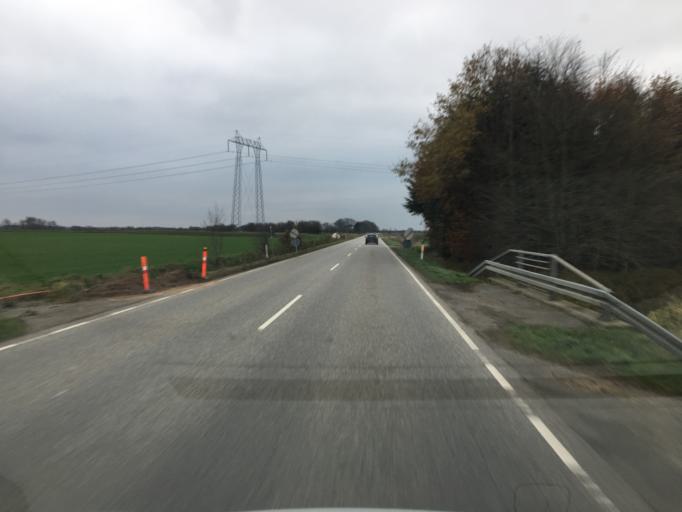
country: DK
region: South Denmark
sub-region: Aabenraa Kommune
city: Rodekro
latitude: 55.0155
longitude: 9.2895
